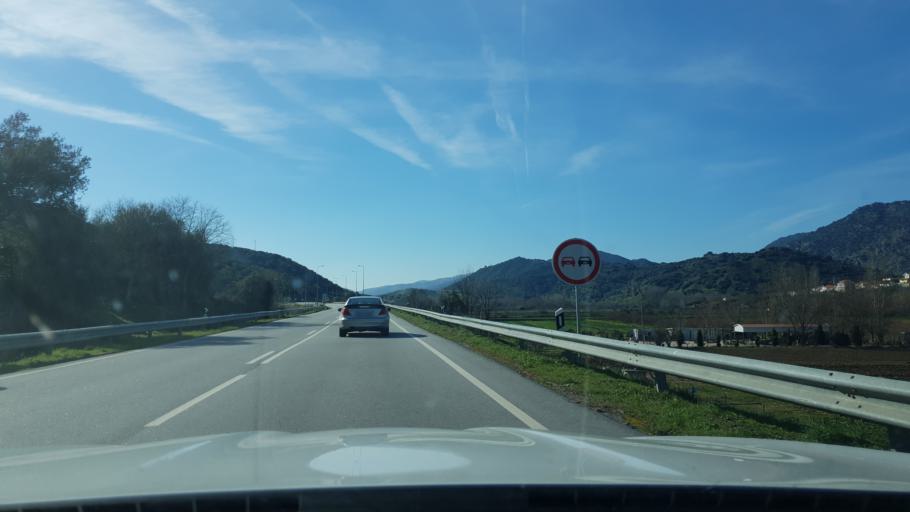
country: PT
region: Braganca
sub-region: Torre de Moncorvo
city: Torre de Moncorvo
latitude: 41.1843
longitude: -7.1018
